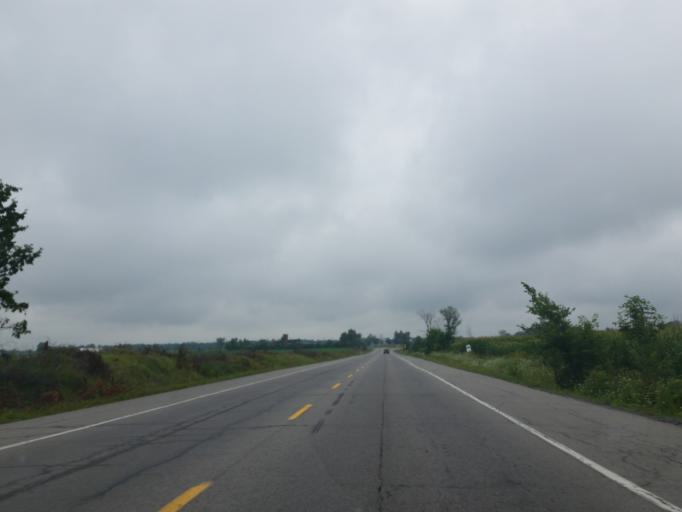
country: CA
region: Ontario
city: Clarence-Rockland
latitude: 45.3420
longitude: -75.3546
